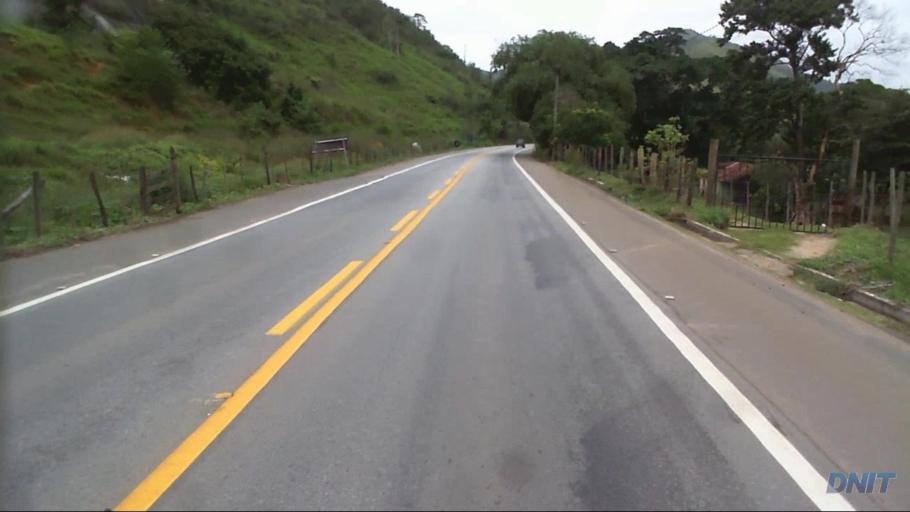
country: BR
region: Minas Gerais
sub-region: Timoteo
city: Timoteo
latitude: -19.5654
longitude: -42.7113
